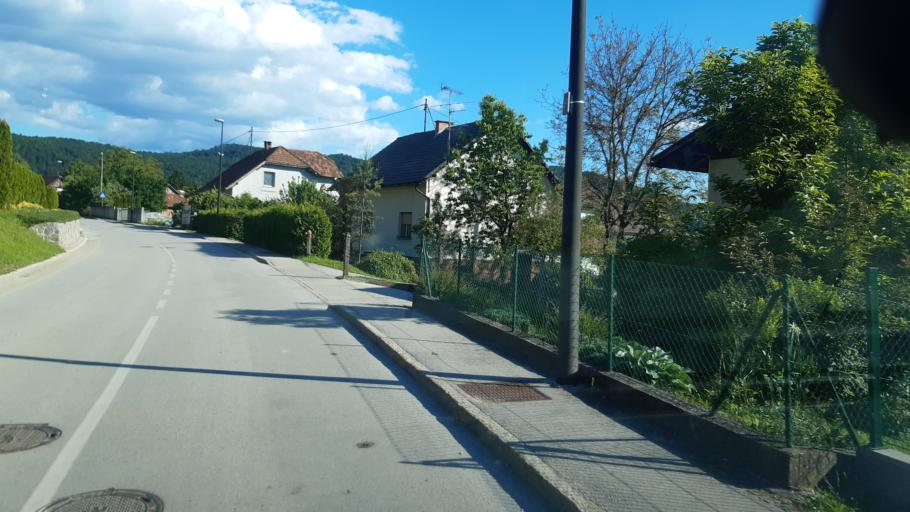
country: SI
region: Vodice
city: Vodice
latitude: 46.1705
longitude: 14.5103
